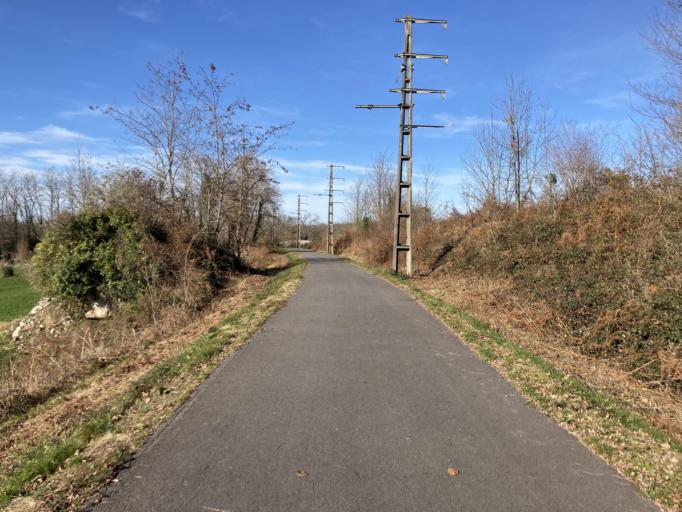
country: FR
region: Aquitaine
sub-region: Departement des Pyrenees-Atlantiques
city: Arudy
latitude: 43.1398
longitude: -0.4487
